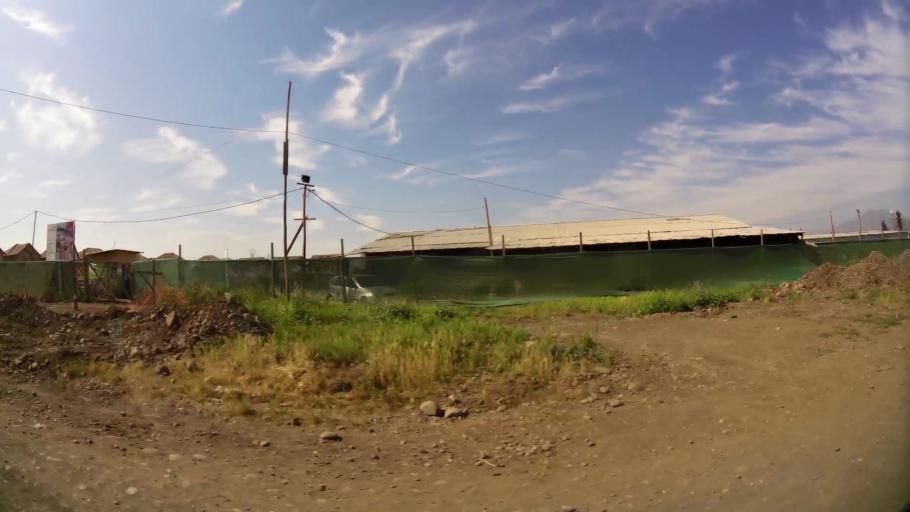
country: CL
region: Santiago Metropolitan
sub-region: Provincia de Talagante
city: Talagante
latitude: -33.6711
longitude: -70.9470
